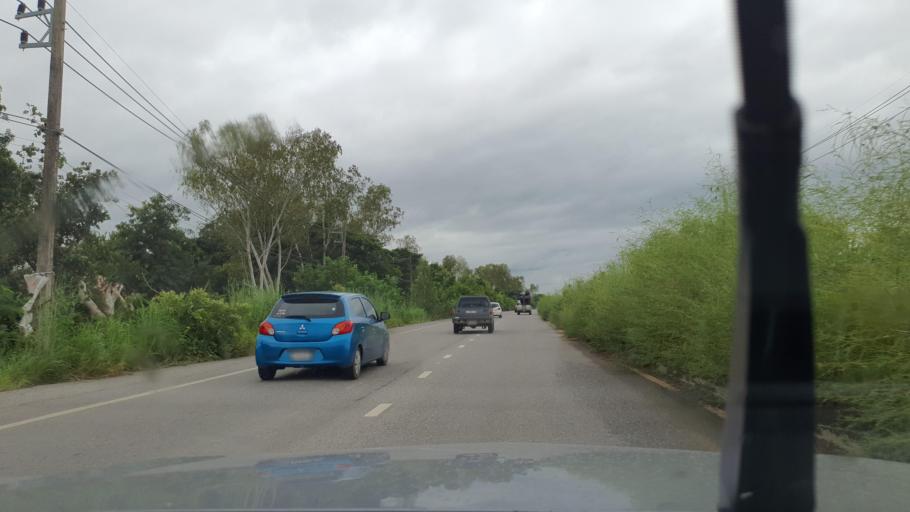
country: TH
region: Lamphun
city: Lamphun
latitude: 18.5998
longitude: 99.0069
